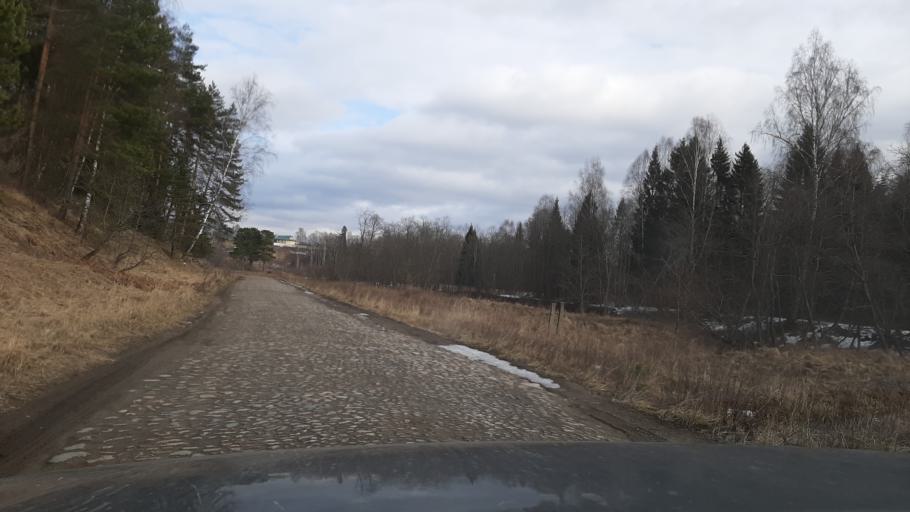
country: RU
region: Ivanovo
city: Teykovo
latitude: 56.8961
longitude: 40.6706
